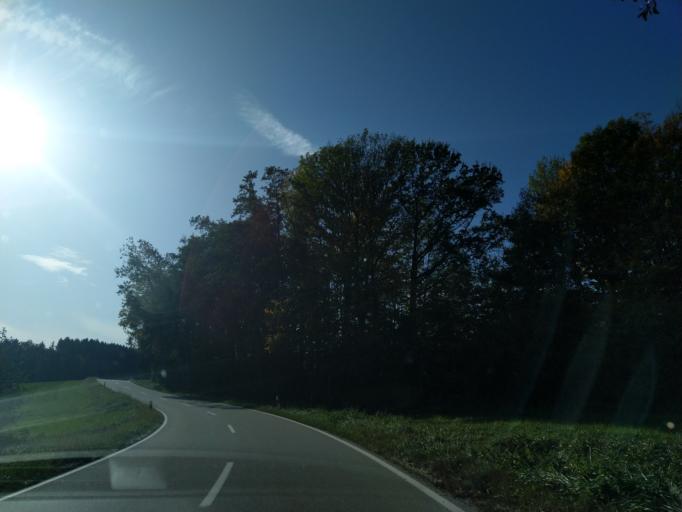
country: DE
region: Bavaria
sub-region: Lower Bavaria
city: Bernried
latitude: 48.9125
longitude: 12.8680
